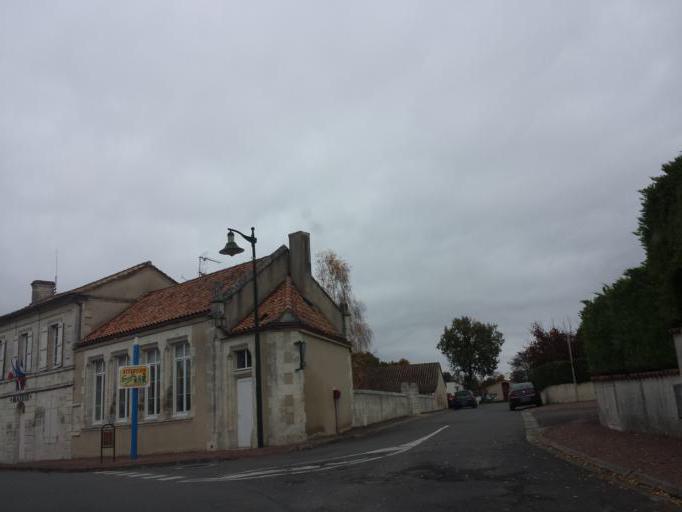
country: FR
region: Poitou-Charentes
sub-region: Departement de la Charente
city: Puymoyen
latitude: 45.6143
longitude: 0.1808
